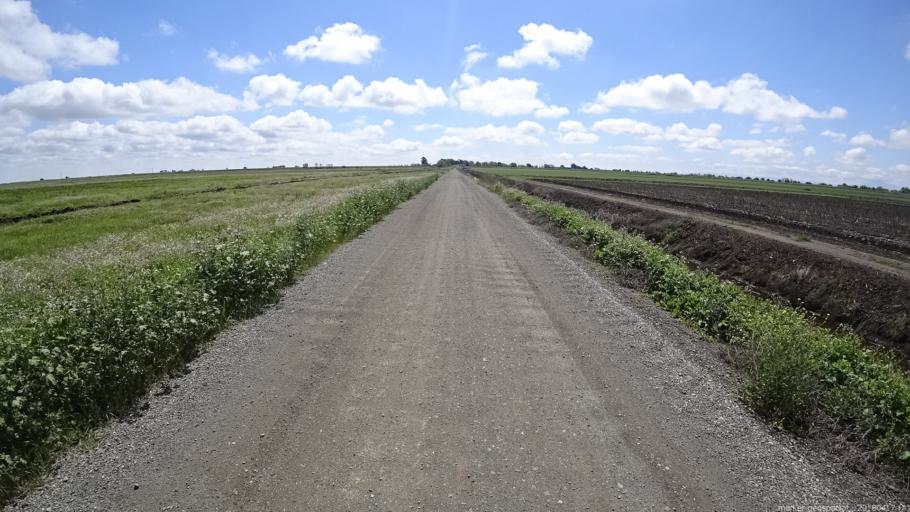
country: US
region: California
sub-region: Solano County
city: Rio Vista
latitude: 38.1401
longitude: -121.5817
